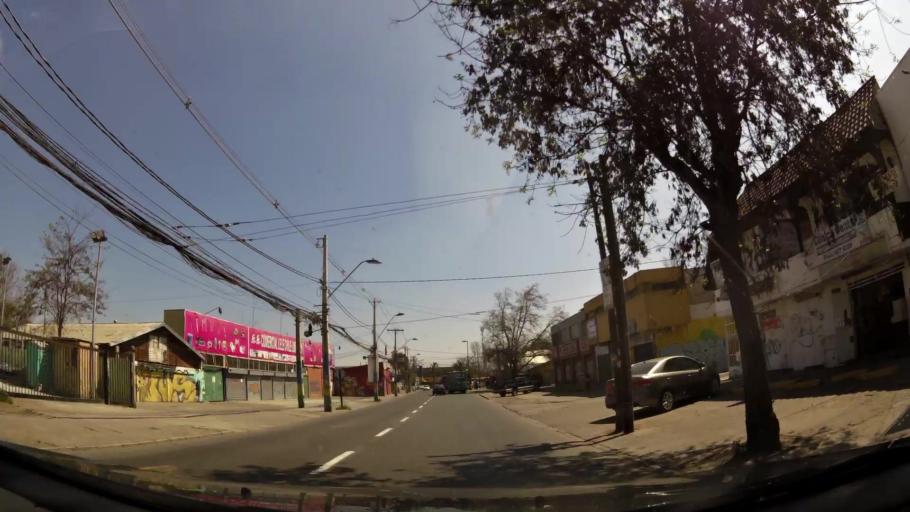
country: CL
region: Santiago Metropolitan
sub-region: Provincia de Santiago
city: Lo Prado
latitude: -33.3666
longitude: -70.7361
